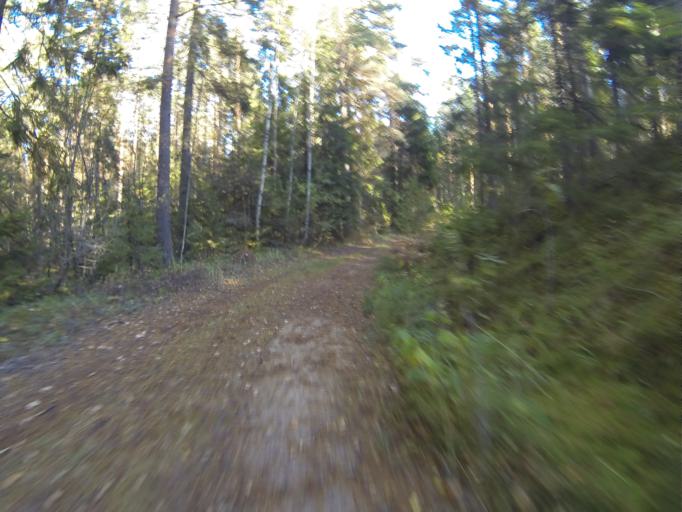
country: FI
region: Varsinais-Suomi
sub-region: Salo
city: Saerkisalo
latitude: 60.2087
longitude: 22.9618
